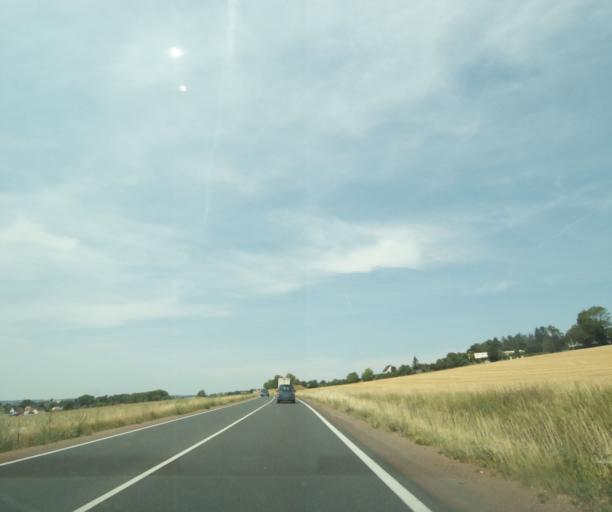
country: FR
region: Poitou-Charentes
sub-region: Departement de la Vienne
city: Chatellerault
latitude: 46.8115
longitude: 0.5676
